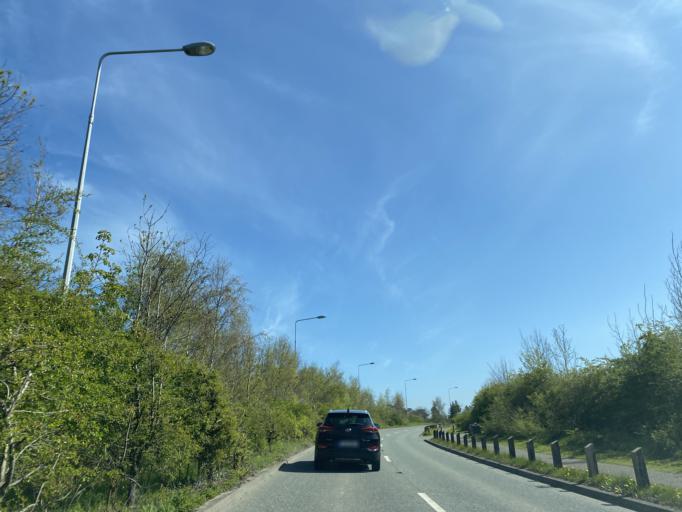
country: IE
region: Leinster
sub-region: Kildare
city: Kill
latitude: 53.2533
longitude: -6.5800
